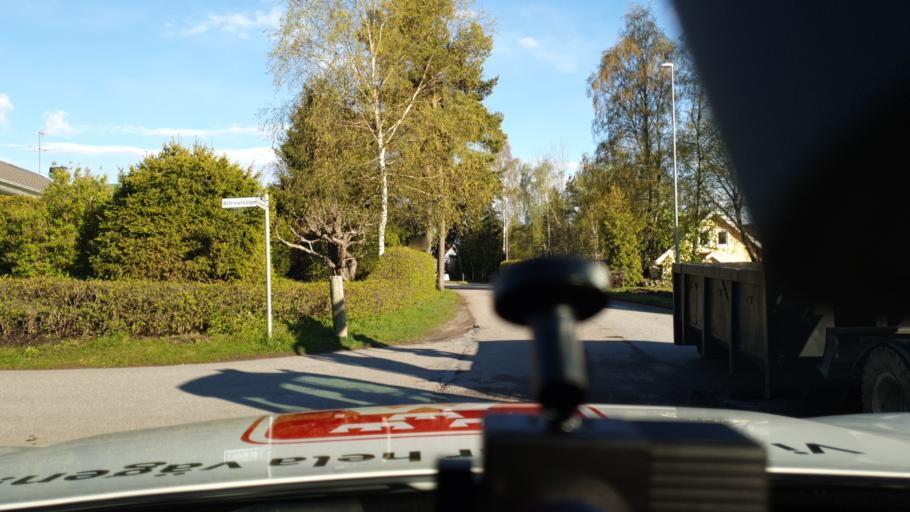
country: SE
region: Stockholm
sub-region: Vallentuna Kommun
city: Vallentuna
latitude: 59.5028
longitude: 18.0815
